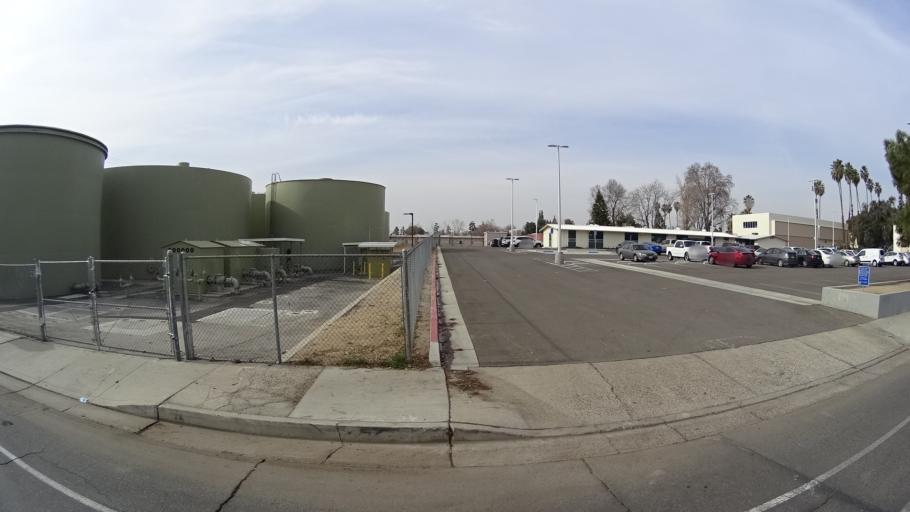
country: US
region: California
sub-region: Kern County
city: Bakersfield
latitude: 35.3853
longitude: -118.9675
